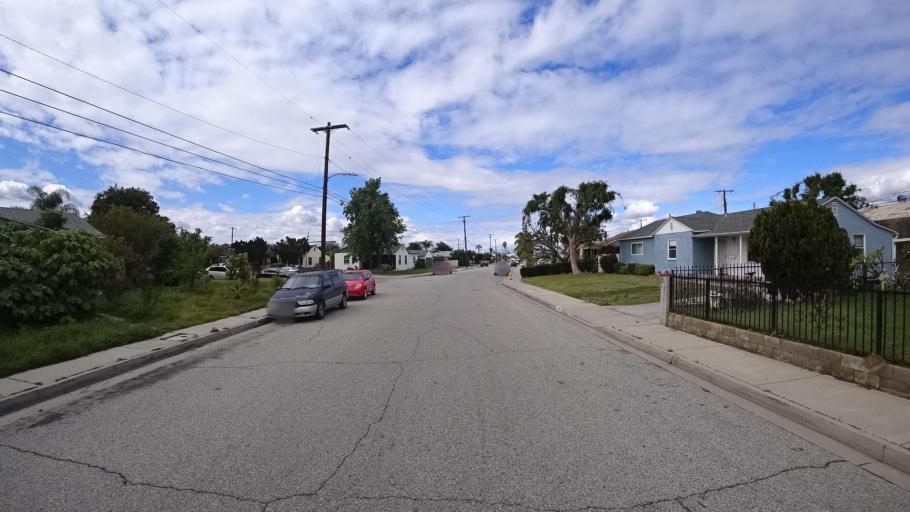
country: US
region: California
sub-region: Los Angeles County
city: Baldwin Park
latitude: 34.1060
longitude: -117.9613
